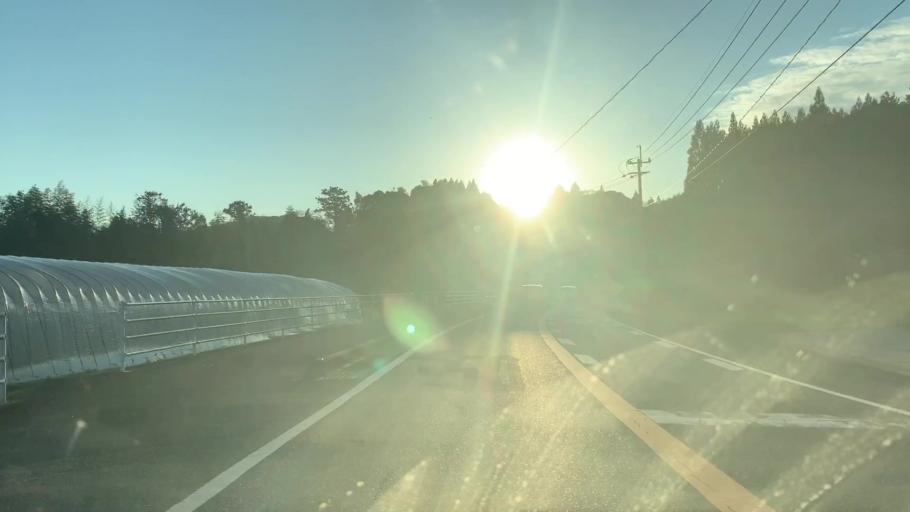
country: JP
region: Saga Prefecture
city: Karatsu
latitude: 33.3421
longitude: 129.9897
